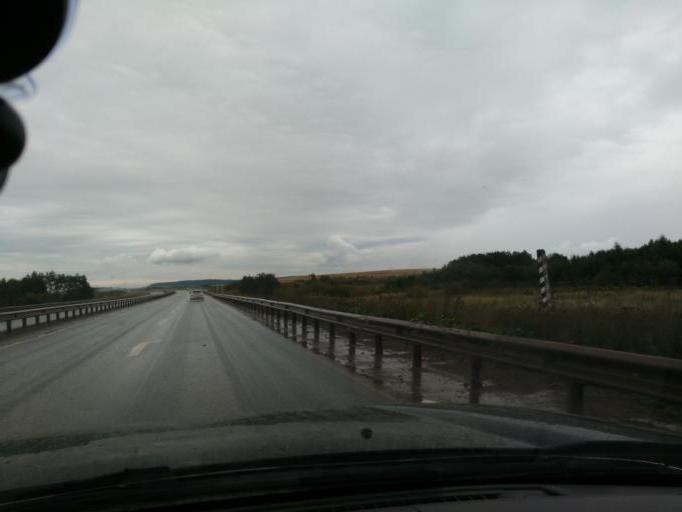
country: RU
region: Perm
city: Kultayevo
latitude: 57.8867
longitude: 55.9331
